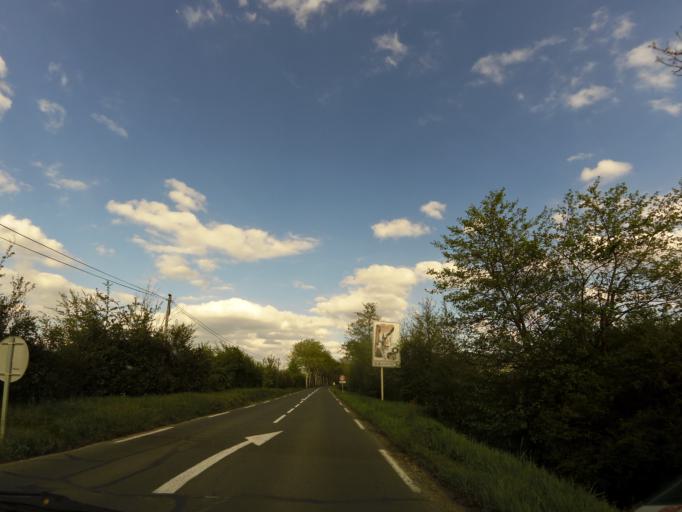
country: FR
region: Midi-Pyrenees
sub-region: Departement de la Haute-Garonne
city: Revel
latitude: 43.4532
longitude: 2.0314
